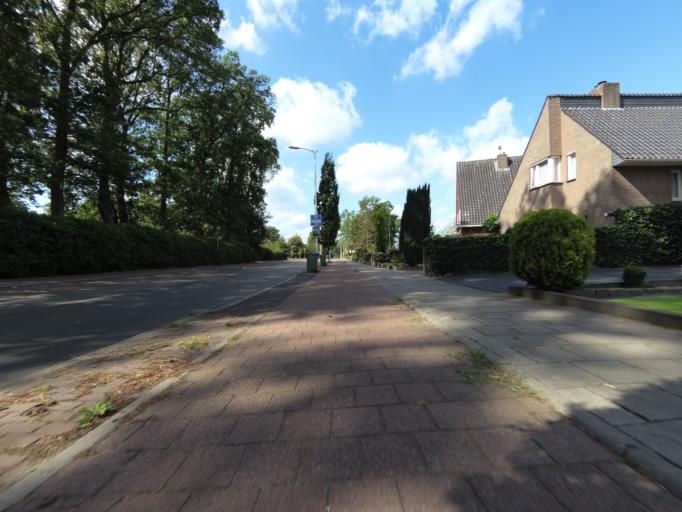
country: NL
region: Overijssel
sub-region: Gemeente Oldenzaal
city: Oldenzaal
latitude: 52.3088
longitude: 6.9180
